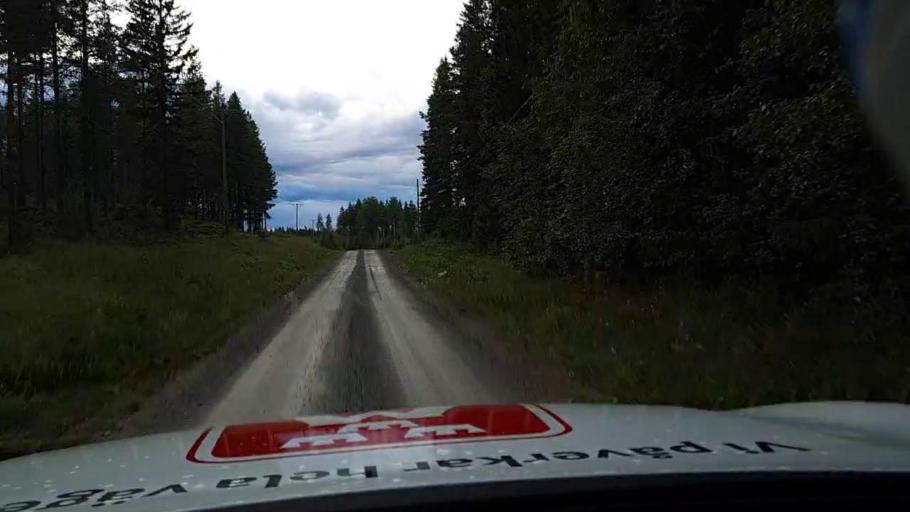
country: SE
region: Jaemtland
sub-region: Bergs Kommun
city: Hoverberg
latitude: 62.8809
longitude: 14.5959
